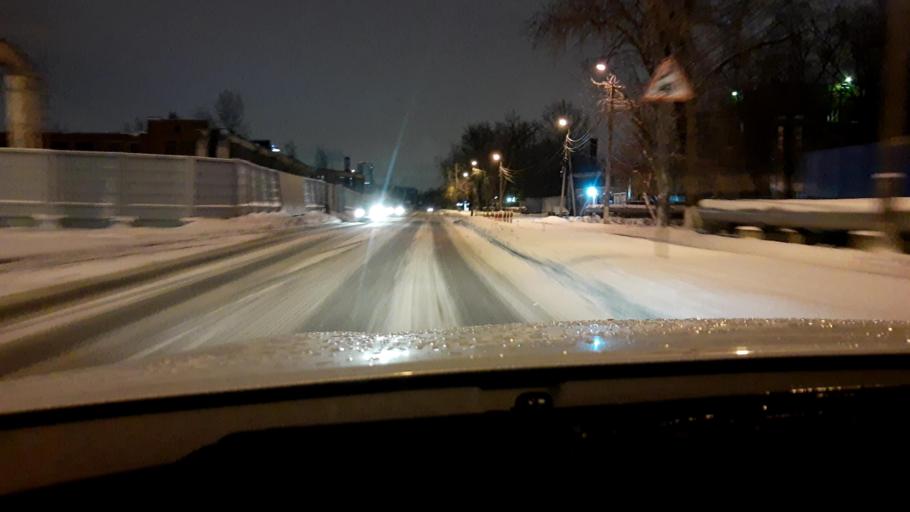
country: RU
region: Moscow
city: Khimki
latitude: 55.9035
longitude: 37.4375
